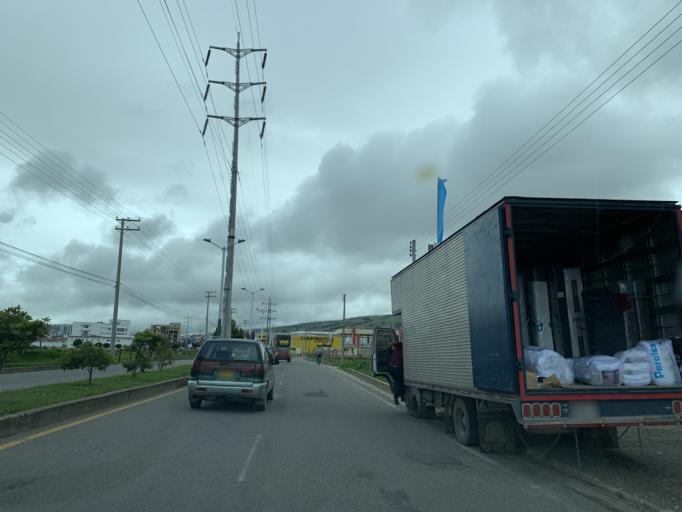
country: CO
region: Boyaca
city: Tunja
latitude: 5.5595
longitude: -73.3433
